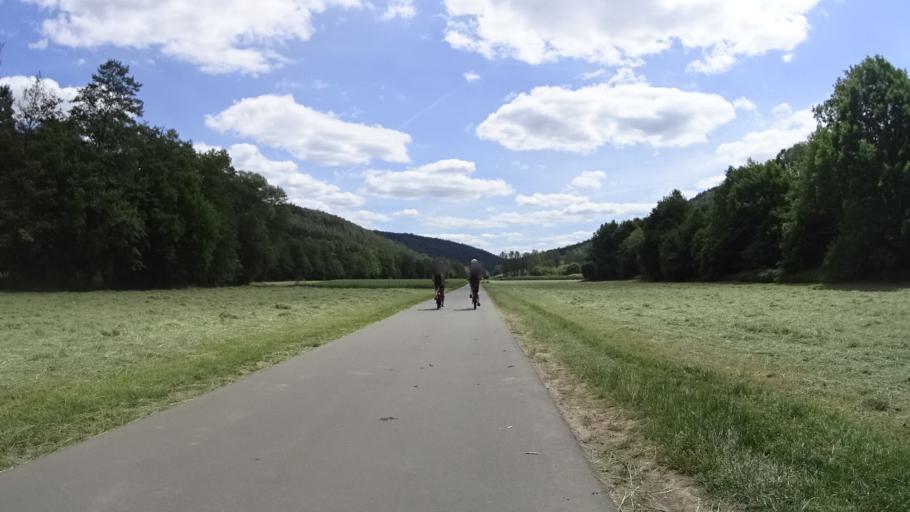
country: DE
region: Bavaria
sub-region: Regierungsbezirk Unterfranken
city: Eichenbuhl
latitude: 49.6960
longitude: 9.3409
